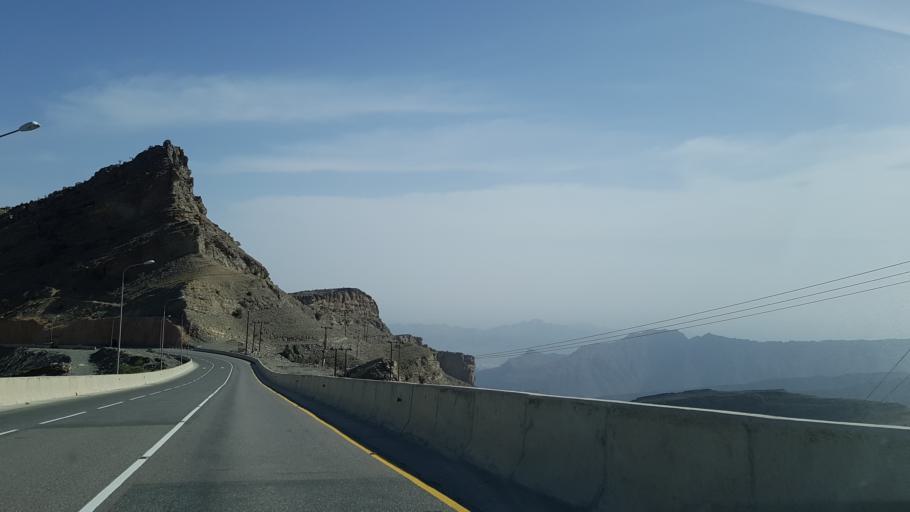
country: OM
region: Muhafazat ad Dakhiliyah
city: Izki
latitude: 23.0171
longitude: 57.6952
